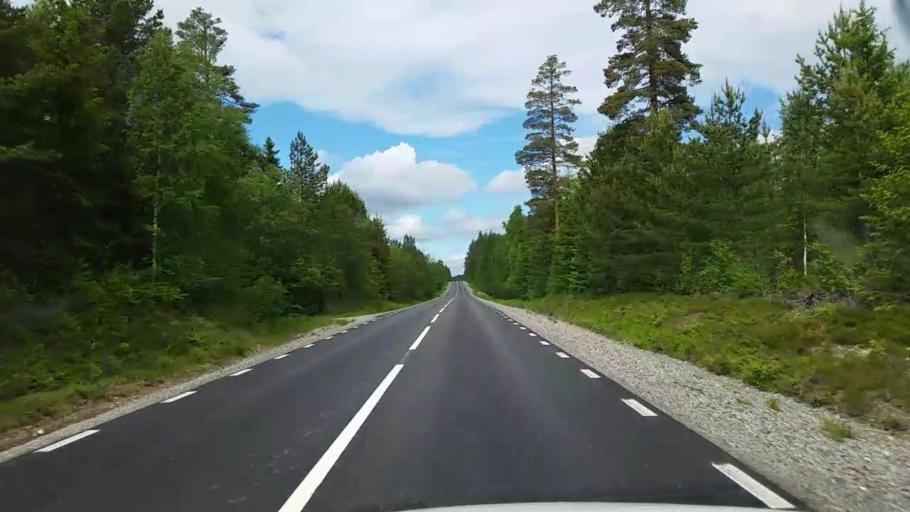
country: SE
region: Gaevleborg
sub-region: Sandvikens Kommun
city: Jarbo
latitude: 60.9072
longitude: 16.3763
